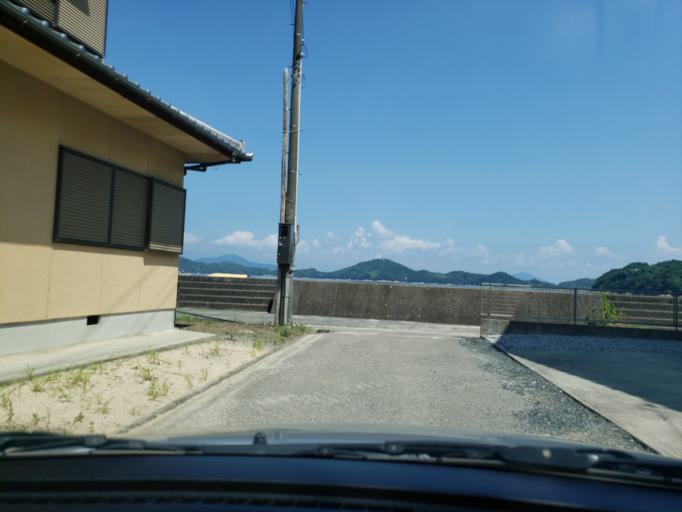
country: JP
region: Ehime
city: Hojo
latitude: 34.0871
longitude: 132.9289
